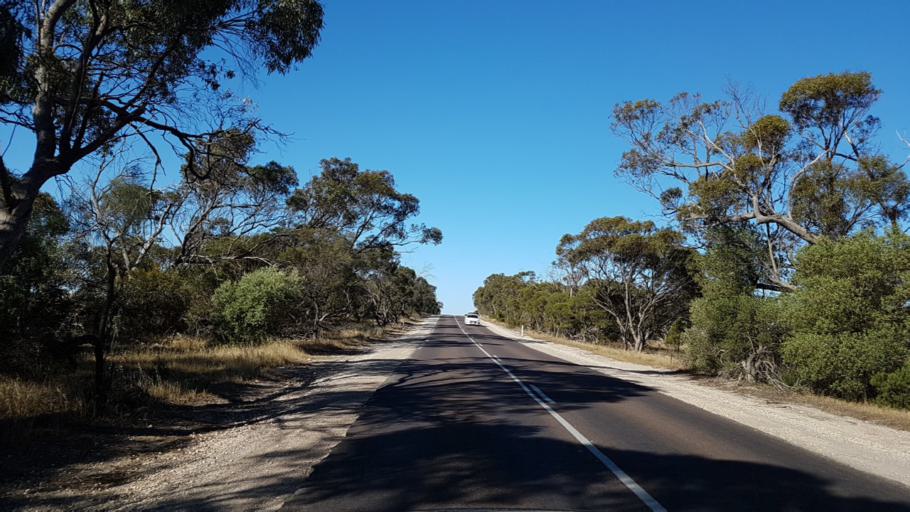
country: AU
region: South Australia
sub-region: Yorke Peninsula
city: Port Victoria
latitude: -34.7409
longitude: 137.6364
